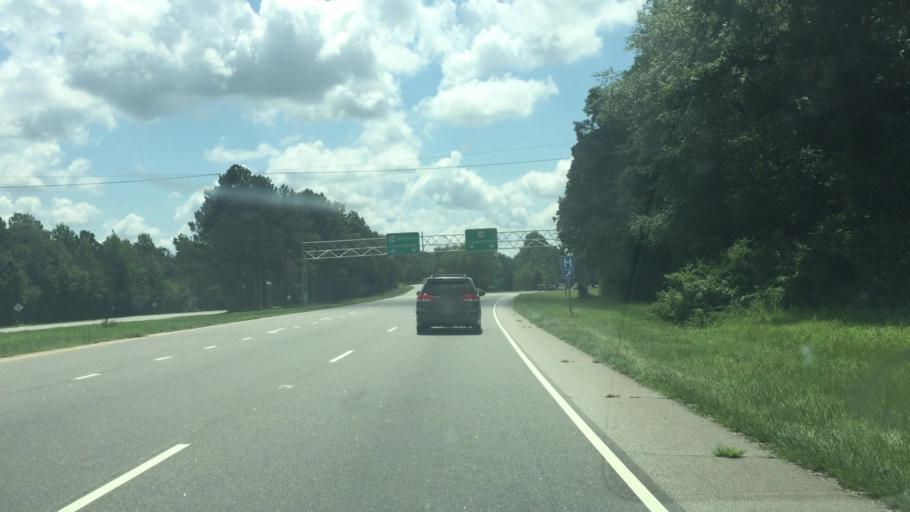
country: US
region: North Carolina
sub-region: Scotland County
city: Laurel Hill
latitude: 34.7898
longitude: -79.5074
